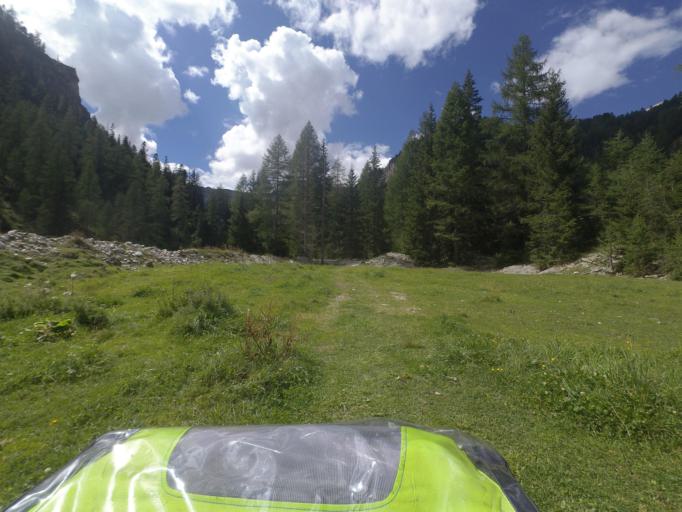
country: AT
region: Salzburg
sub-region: Politischer Bezirk Sankt Johann im Pongau
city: Kleinarl
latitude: 47.1874
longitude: 13.3733
